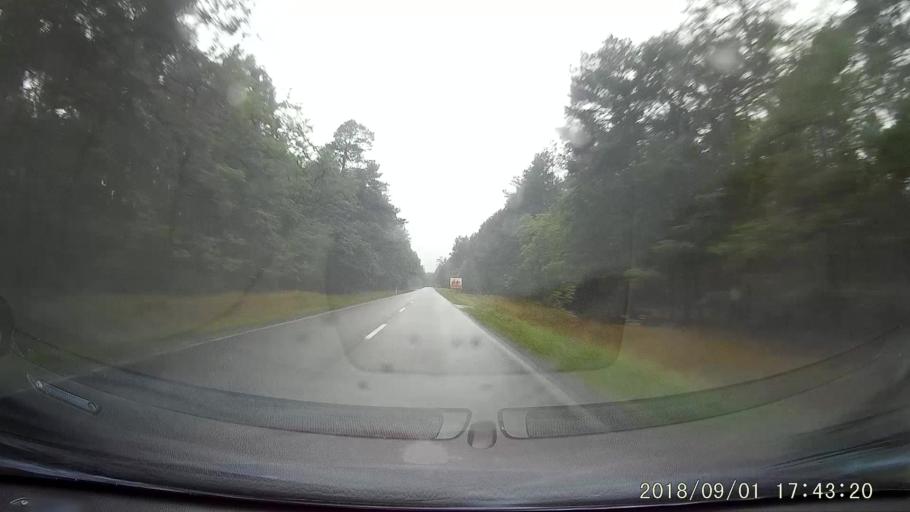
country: PL
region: Lubusz
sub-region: Powiat zaganski
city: Ilowa
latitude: 51.5456
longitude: 15.2510
